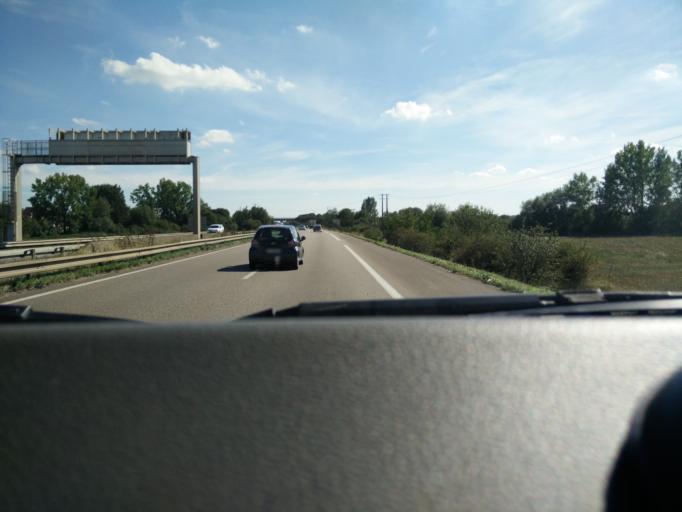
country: FR
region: Lorraine
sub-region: Departement de la Moselle
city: Bertrange
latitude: 49.3129
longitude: 6.1823
